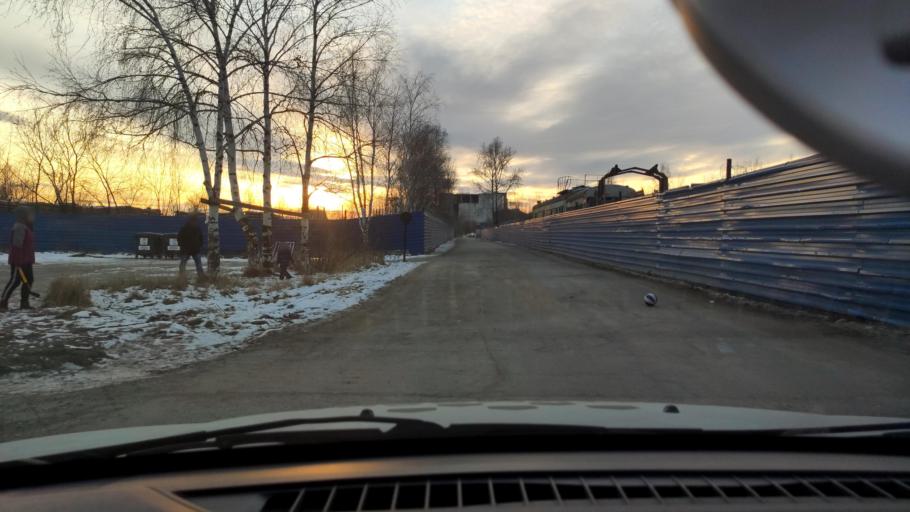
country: RU
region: Perm
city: Kondratovo
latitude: 58.0343
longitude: 56.0645
